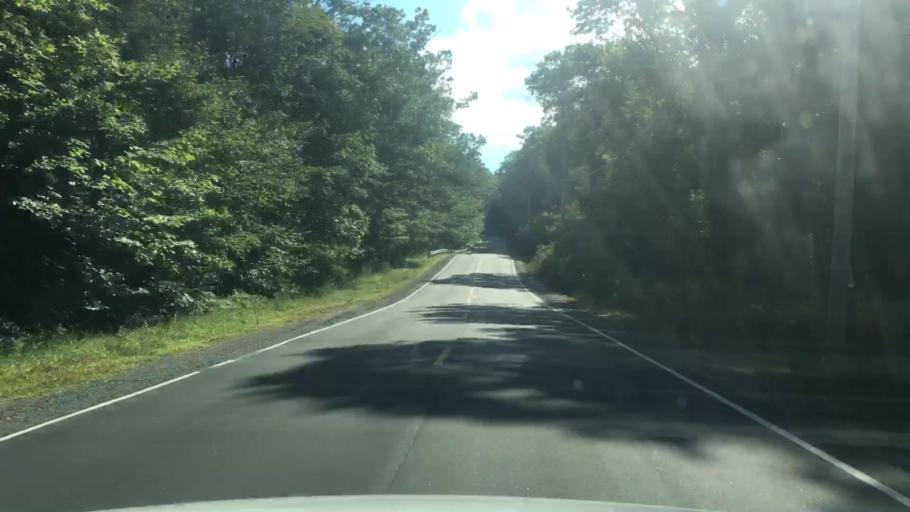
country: US
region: Maine
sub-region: Kennebec County
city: Mount Vernon
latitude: 44.4813
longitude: -70.0004
